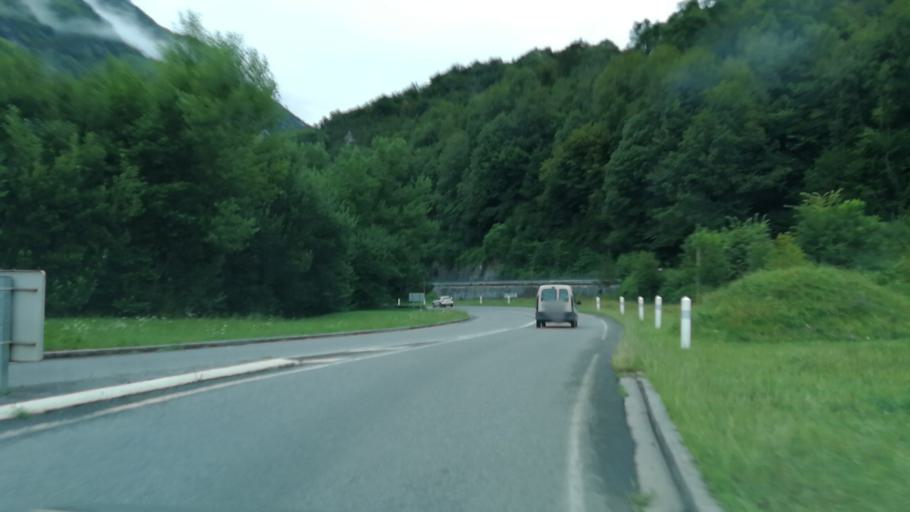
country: FR
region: Aquitaine
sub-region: Departement des Pyrenees-Atlantiques
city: Arette
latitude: 43.0110
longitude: -0.6028
